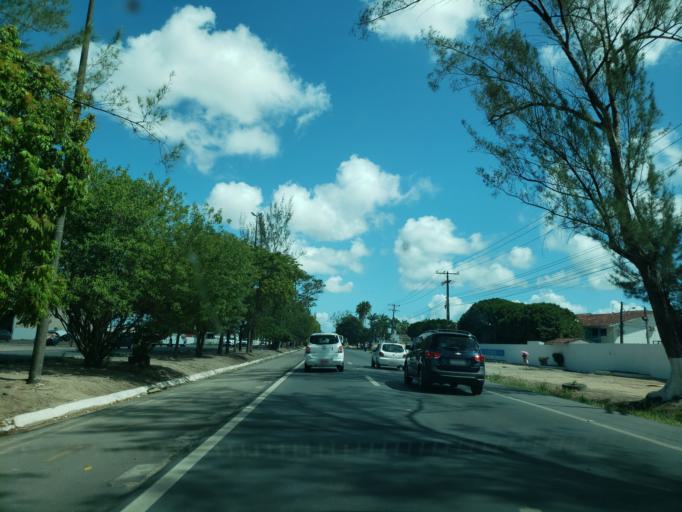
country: BR
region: Alagoas
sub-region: Satuba
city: Satuba
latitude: -9.5487
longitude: -35.7866
